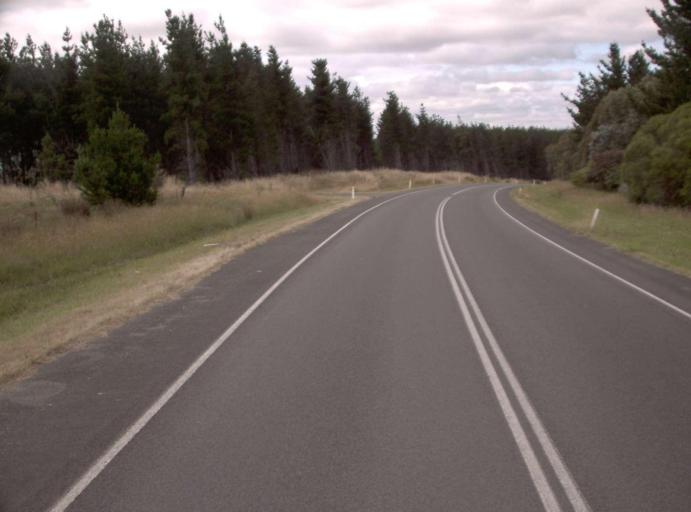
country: AU
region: Victoria
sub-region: Latrobe
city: Morwell
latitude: -38.1952
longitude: 146.4496
